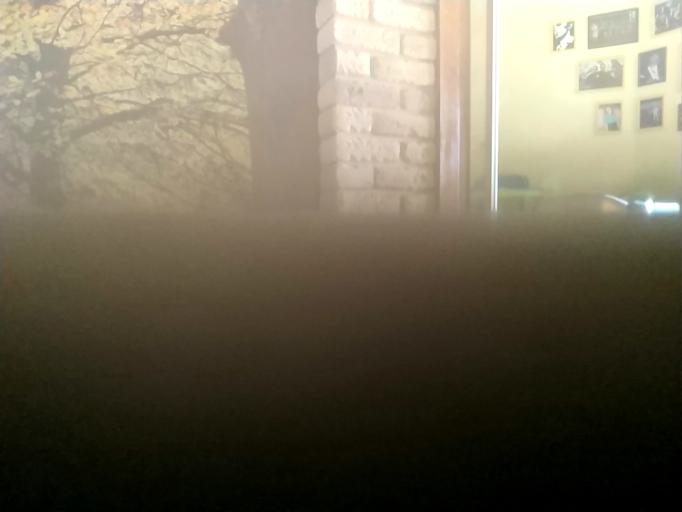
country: RU
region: Kaluga
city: Yukhnov
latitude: 54.7443
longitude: 35.0348
